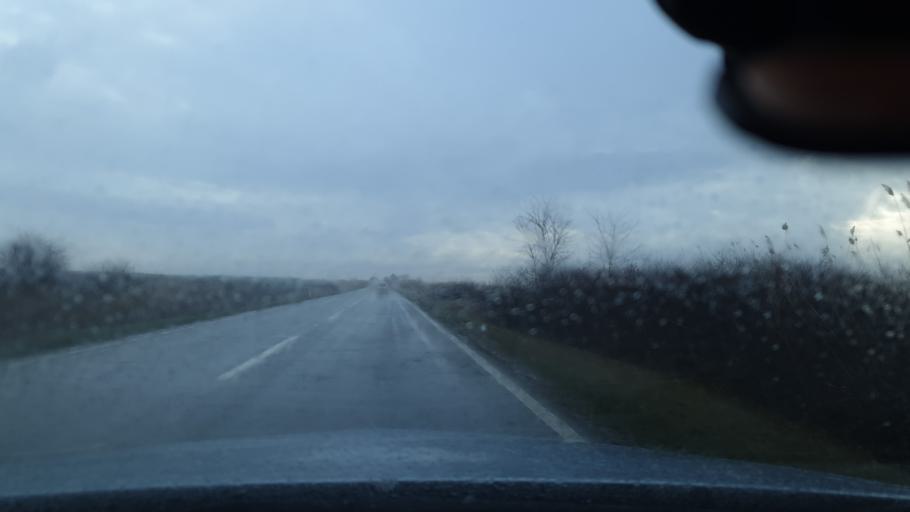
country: RS
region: Autonomna Pokrajina Vojvodina
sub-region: Juznobanatski Okrug
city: Pancevo
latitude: 44.8364
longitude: 20.8125
